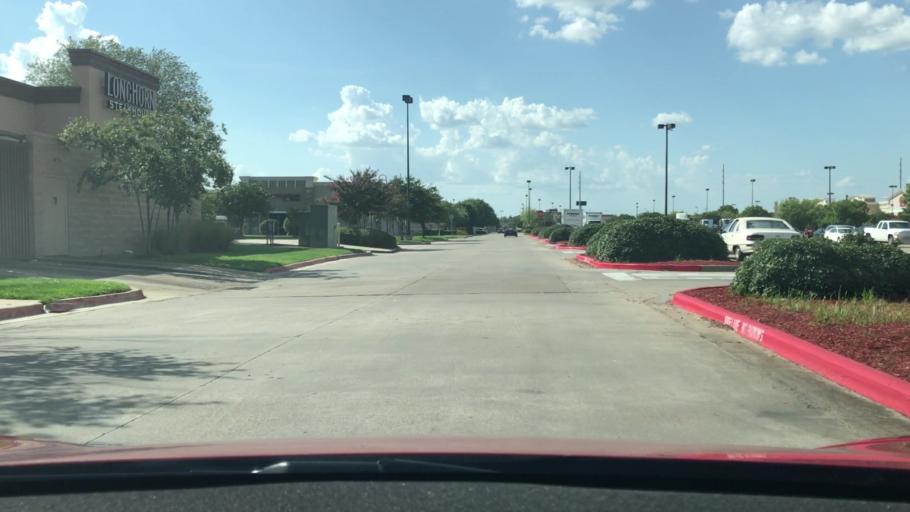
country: US
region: Louisiana
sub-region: Bossier Parish
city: Bossier City
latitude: 32.4396
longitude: -93.7152
